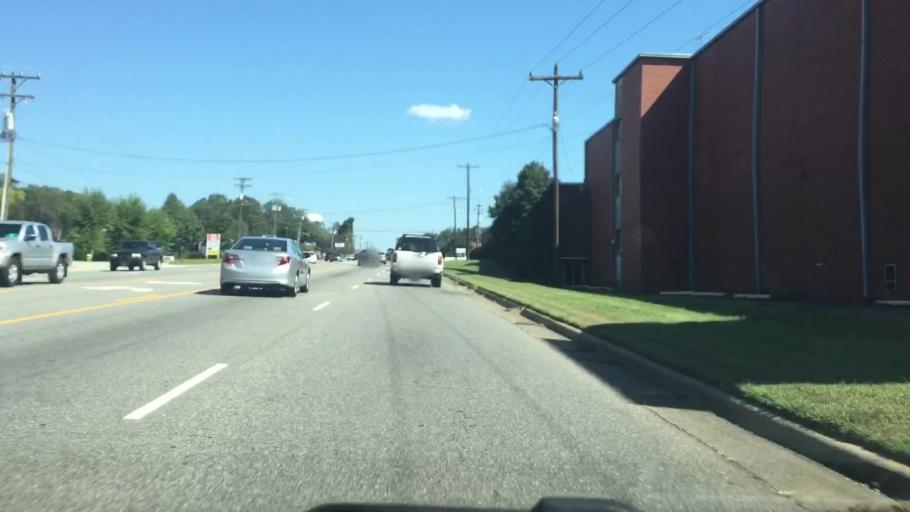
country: US
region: North Carolina
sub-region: Iredell County
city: Mooresville
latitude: 35.5914
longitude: -80.8227
